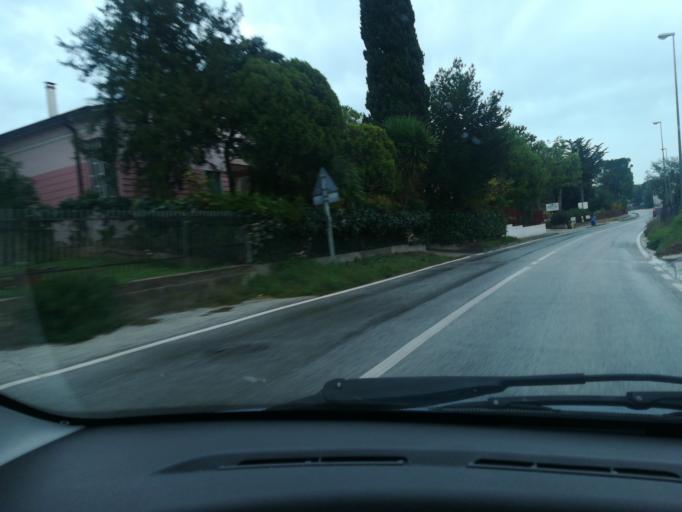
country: IT
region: The Marches
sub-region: Provincia di Macerata
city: Santa Maria Apparente
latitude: 43.2965
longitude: 13.6852
